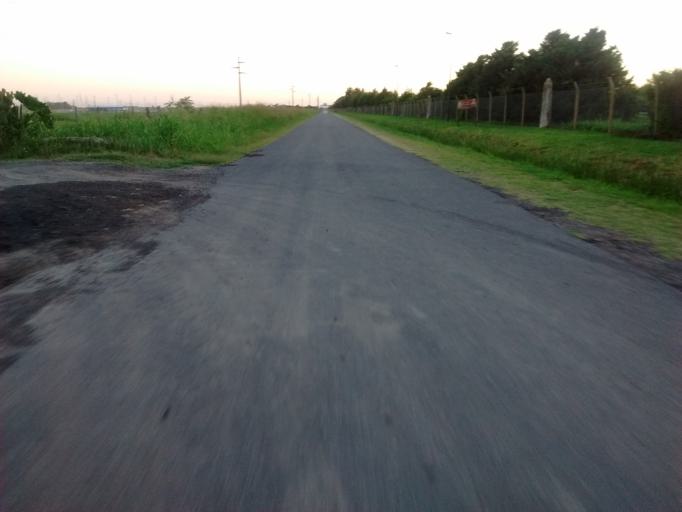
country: AR
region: Santa Fe
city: Funes
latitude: -32.9451
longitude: -60.8196
